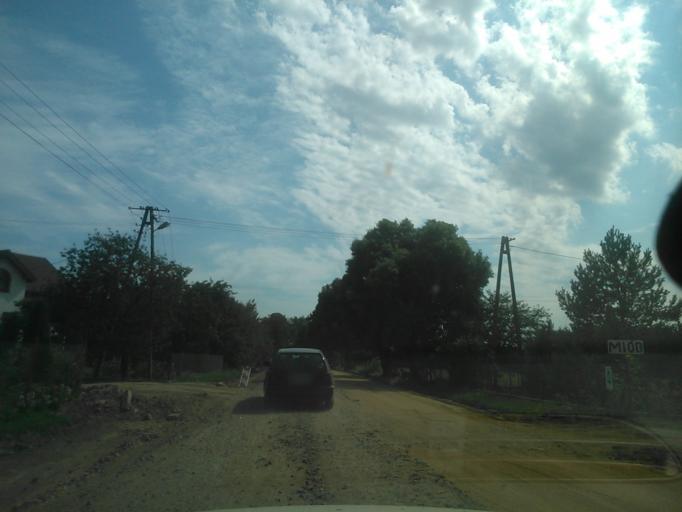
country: PL
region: Warmian-Masurian Voivodeship
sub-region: Powiat dzialdowski
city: Ilowo -Osada
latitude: 53.1989
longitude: 20.2491
